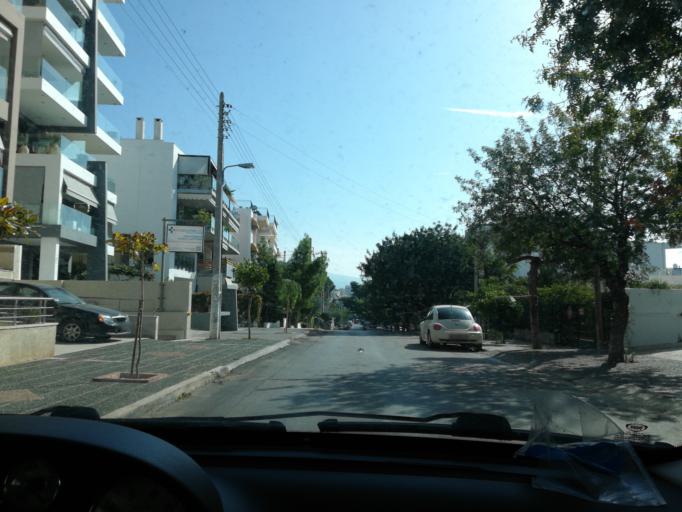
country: GR
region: Attica
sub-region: Nomarchia Athinas
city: Alimos
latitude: 37.9158
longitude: 23.7134
